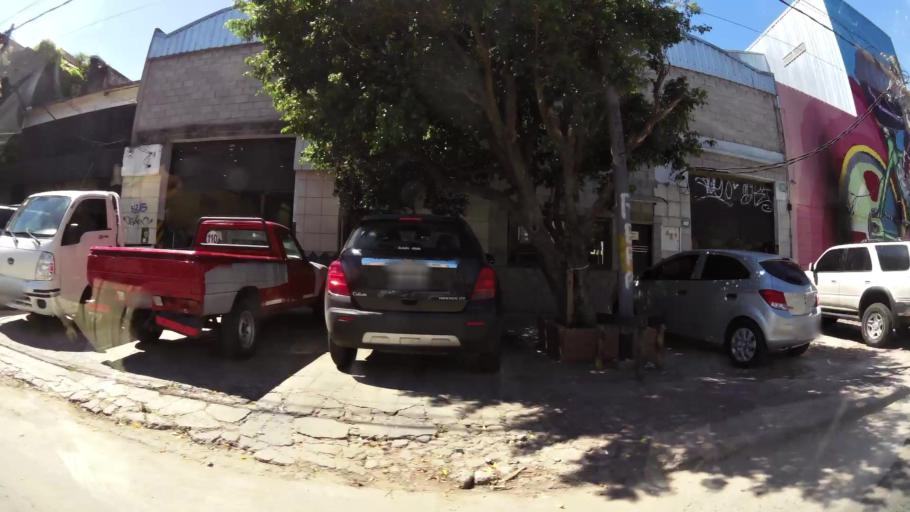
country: AR
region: Buenos Aires
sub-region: Partido de General San Martin
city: General San Martin
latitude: -34.5798
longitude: -58.5315
